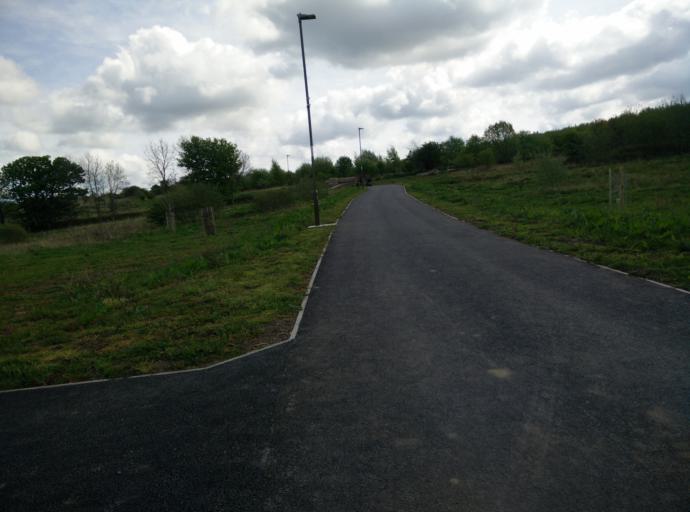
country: GB
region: Scotland
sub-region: West Lothian
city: Seafield
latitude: 55.9225
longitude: -3.1249
